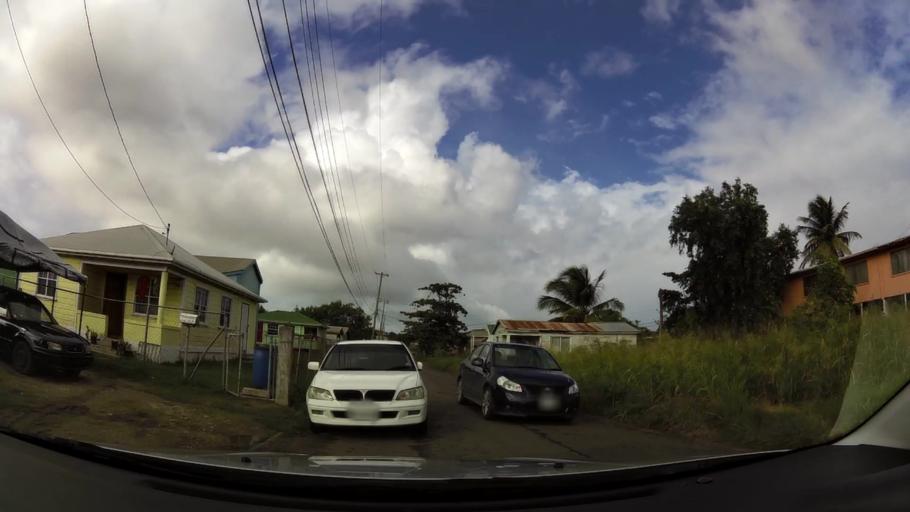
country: AG
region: Saint John
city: Saint John's
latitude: 17.1215
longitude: -61.8245
